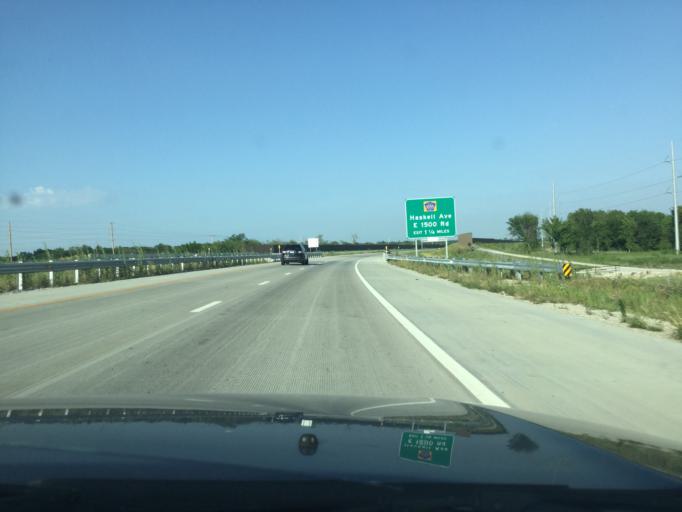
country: US
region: Kansas
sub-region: Douglas County
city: Lawrence
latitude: 38.9260
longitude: -95.2430
